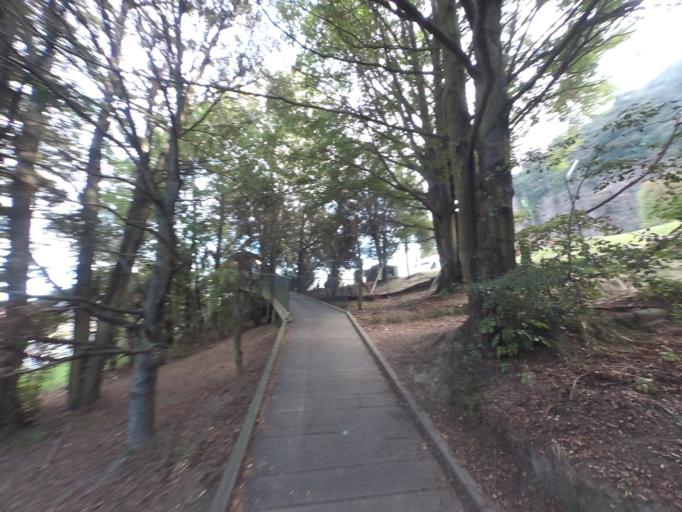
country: NZ
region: Otago
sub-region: Queenstown-Lakes District
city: Queenstown
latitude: -45.0286
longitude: 168.6566
